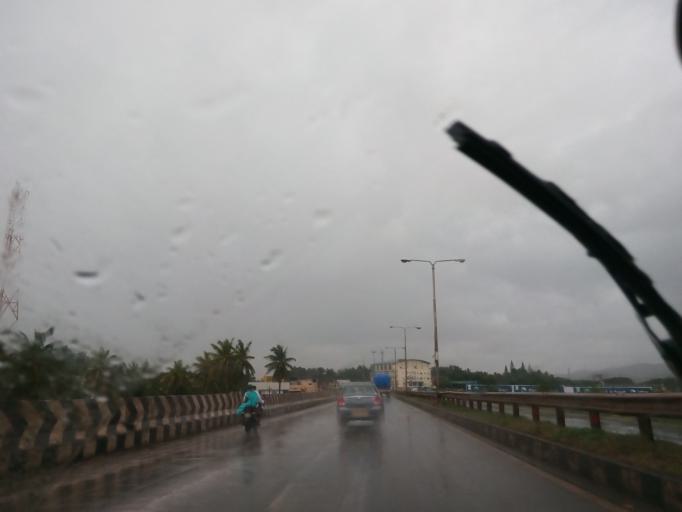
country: IN
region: Karnataka
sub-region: Chitradurga
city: Chitradurga
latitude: 14.2374
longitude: 76.3812
